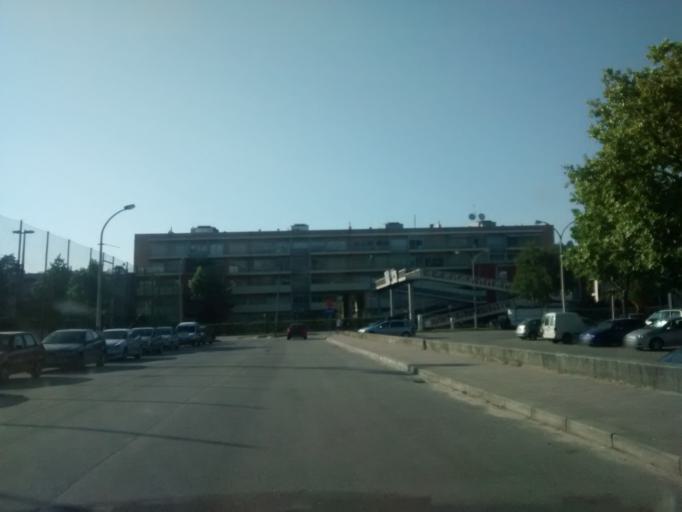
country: PT
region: Braga
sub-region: Braga
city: Braga
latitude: 41.5544
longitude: -8.4006
